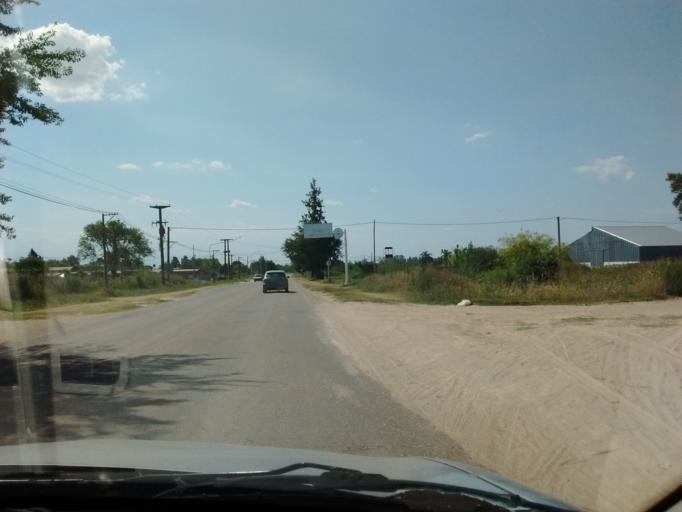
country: AR
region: Entre Rios
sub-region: Departamento de Victoria
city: Victoria
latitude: -32.6090
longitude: -60.1445
